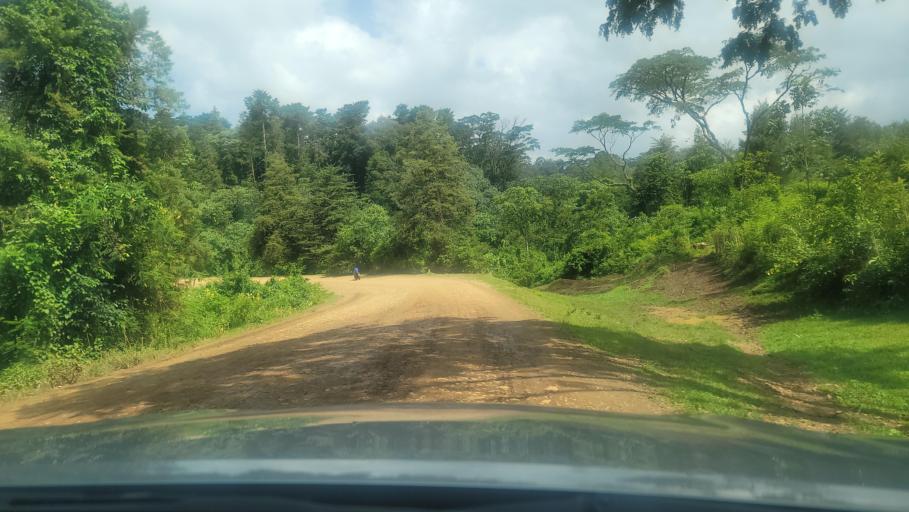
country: ET
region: Oromiya
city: Agaro
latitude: 7.7914
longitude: 36.4322
